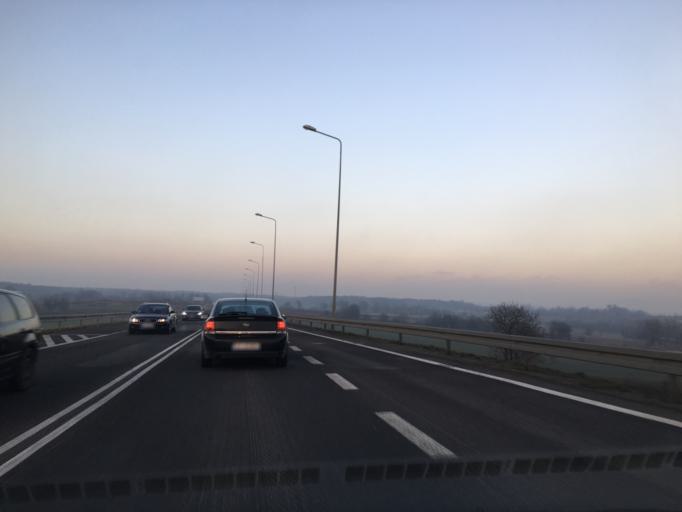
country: PL
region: Silesian Voivodeship
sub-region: Powiat tarnogorski
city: Radzionkow
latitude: 50.3579
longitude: 18.8682
